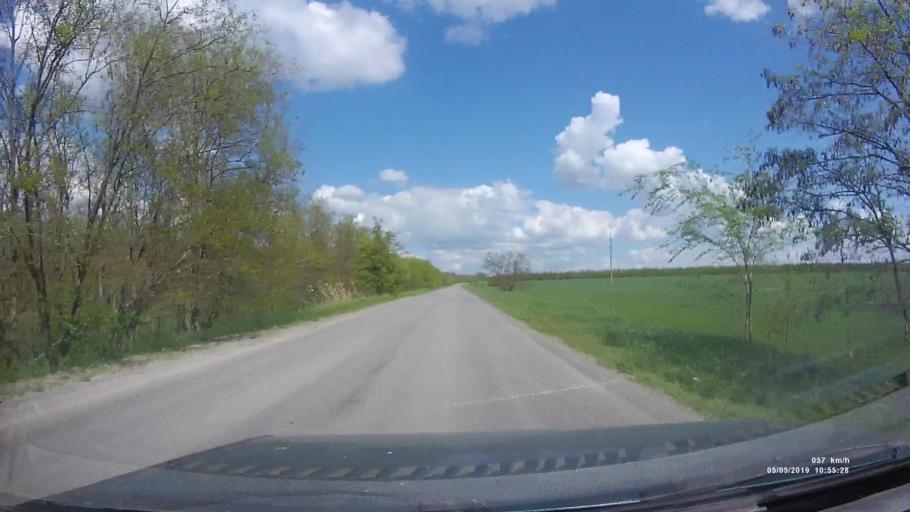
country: RU
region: Rostov
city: Ust'-Donetskiy
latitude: 47.6658
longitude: 40.8211
